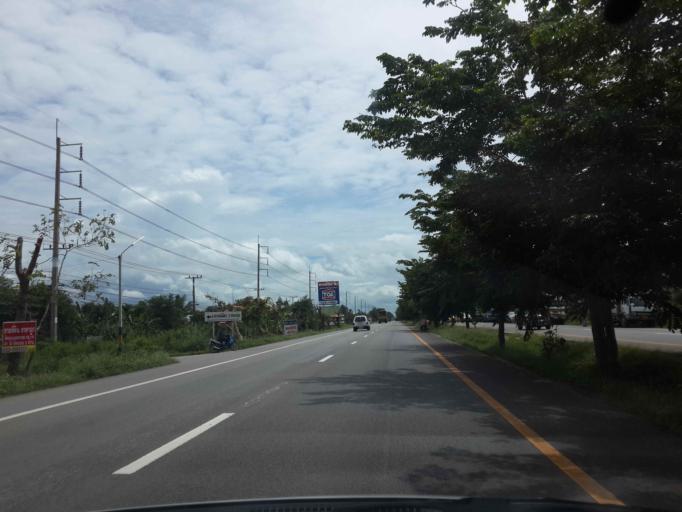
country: TH
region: Ratchaburi
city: Pak Tho
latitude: 13.4066
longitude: 99.8129
